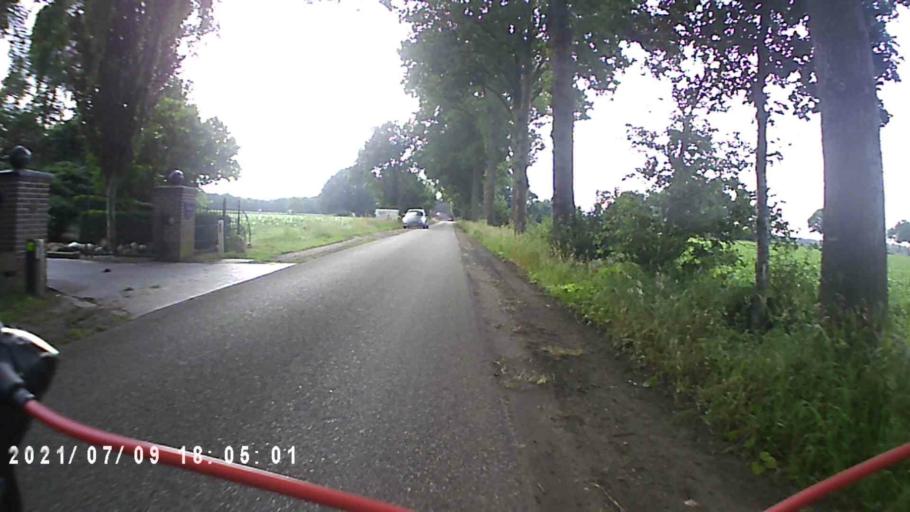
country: NL
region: Groningen
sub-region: Gemeente Pekela
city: Oude Pekela
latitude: 53.0676
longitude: 7.0356
